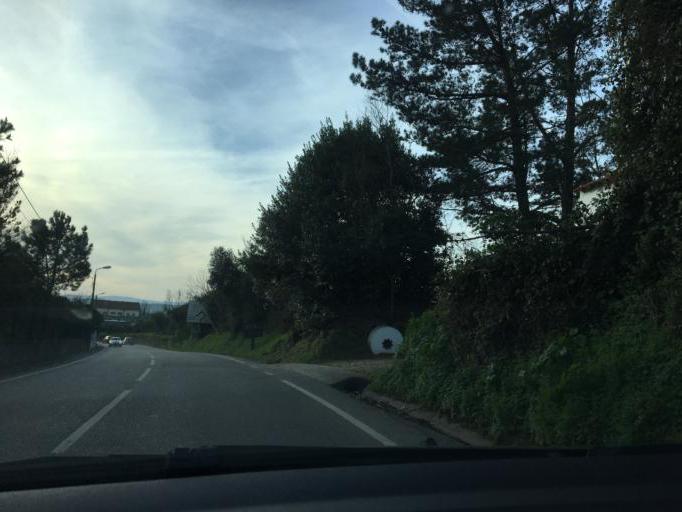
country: PT
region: Coimbra
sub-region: Montemor-O-Velho
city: Montemor-o-Velho
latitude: 40.2008
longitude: -8.6474
